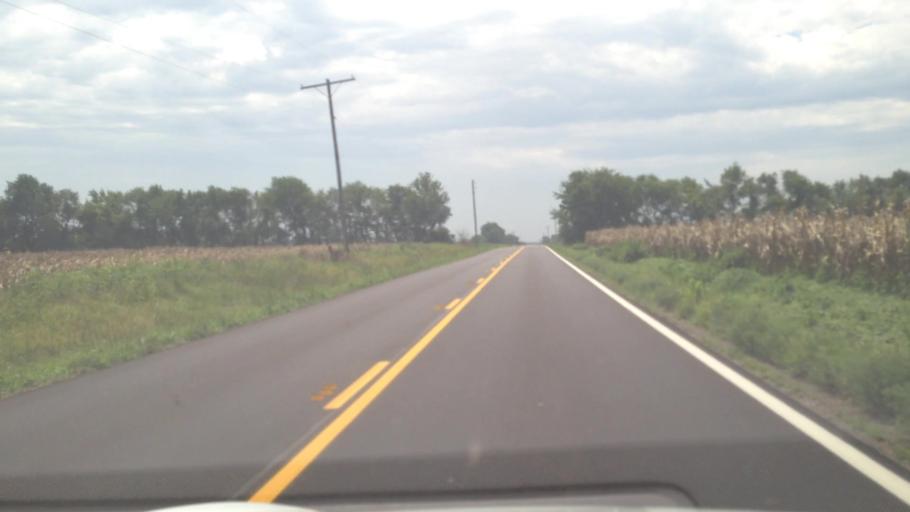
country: US
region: Kansas
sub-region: Crawford County
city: Girard
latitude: 37.6398
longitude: -94.9699
